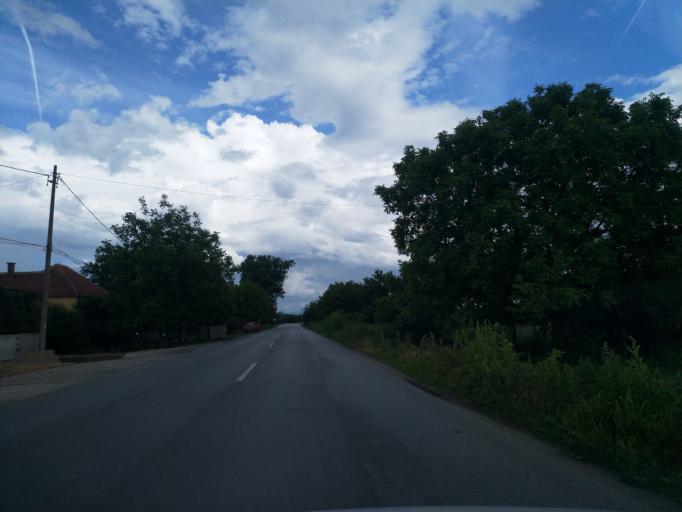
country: RS
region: Central Serbia
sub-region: Pomoravski Okrug
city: Cuprija
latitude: 43.9463
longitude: 21.3383
